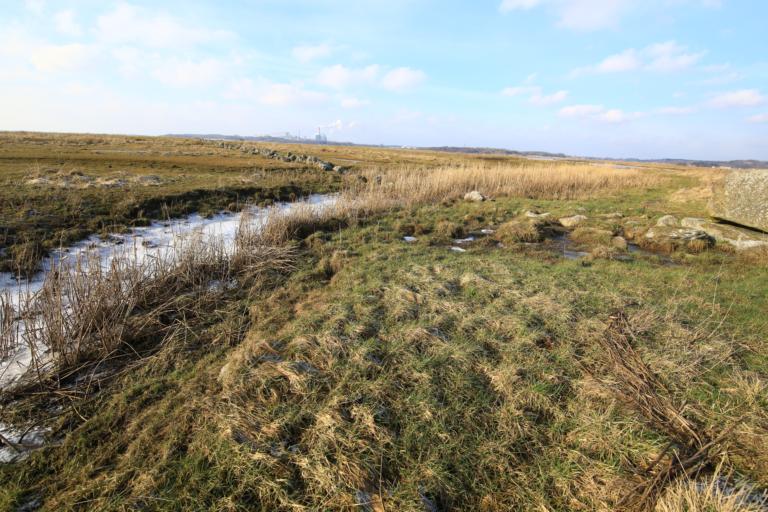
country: SE
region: Halland
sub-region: Varbergs Kommun
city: Veddige
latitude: 57.2162
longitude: 12.2175
